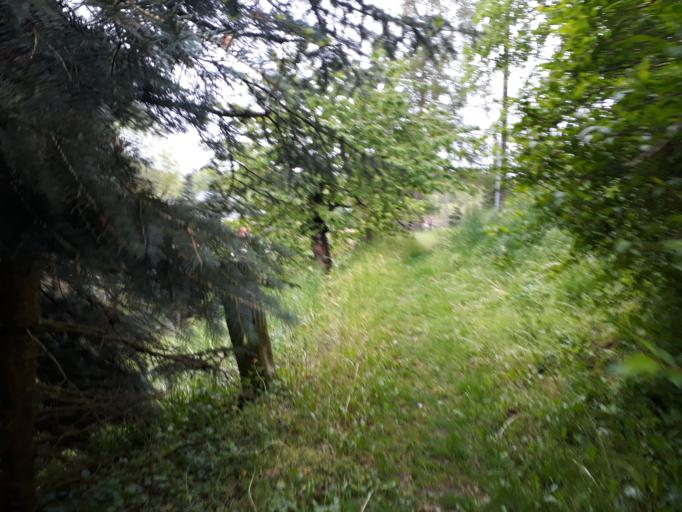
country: DE
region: Saxony
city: Reinhardtsgrimma
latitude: 50.8913
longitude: 13.7479
